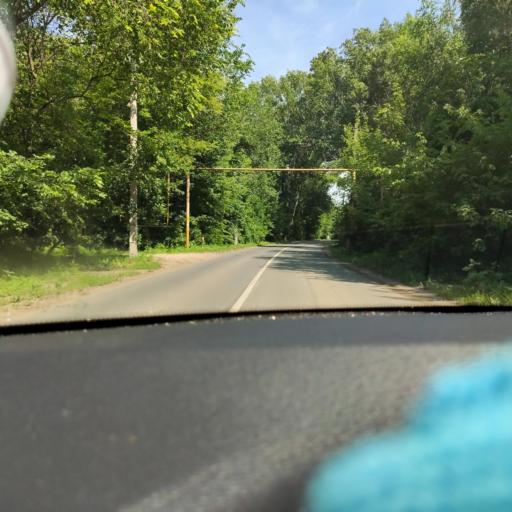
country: RU
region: Samara
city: Novokuybyshevsk
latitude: 53.1583
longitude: 49.9483
